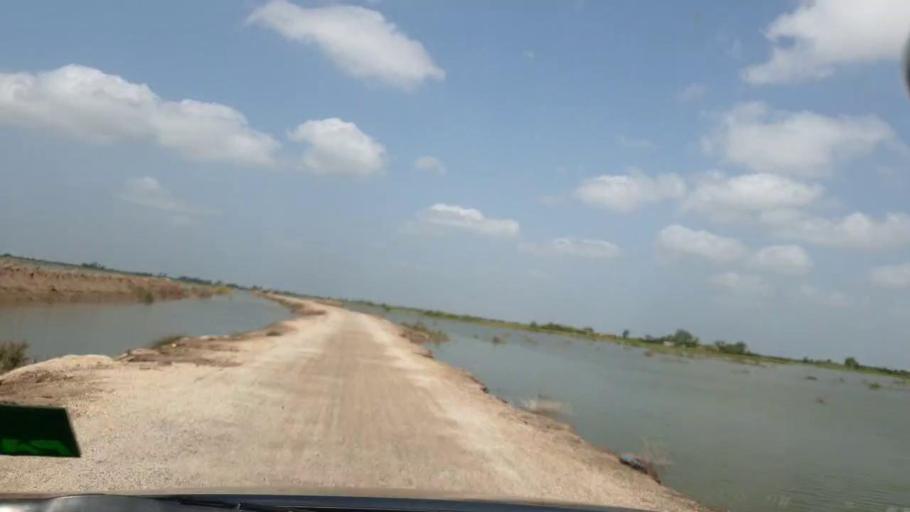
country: PK
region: Sindh
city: Kadhan
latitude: 24.5922
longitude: 69.1343
